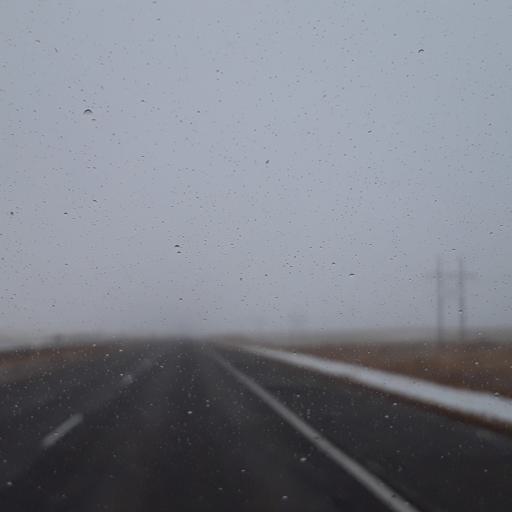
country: US
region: Colorado
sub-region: Logan County
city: Sterling
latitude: 40.7756
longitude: -102.9264
